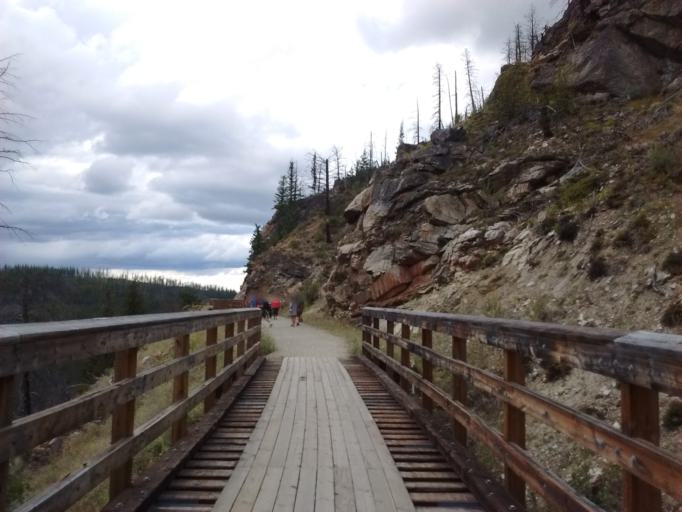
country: CA
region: British Columbia
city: Kelowna
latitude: 49.7880
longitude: -119.3088
